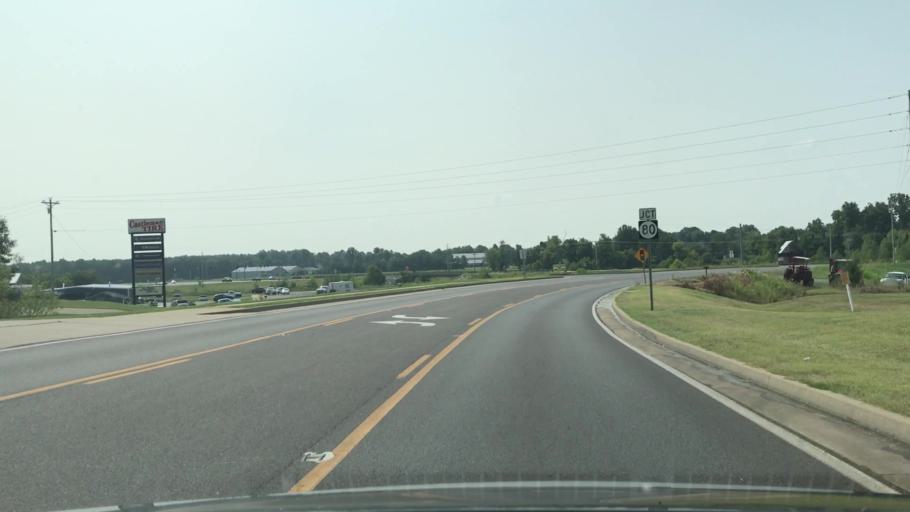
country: US
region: Kentucky
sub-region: Graves County
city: Mayfield
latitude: 36.7183
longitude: -88.6250
